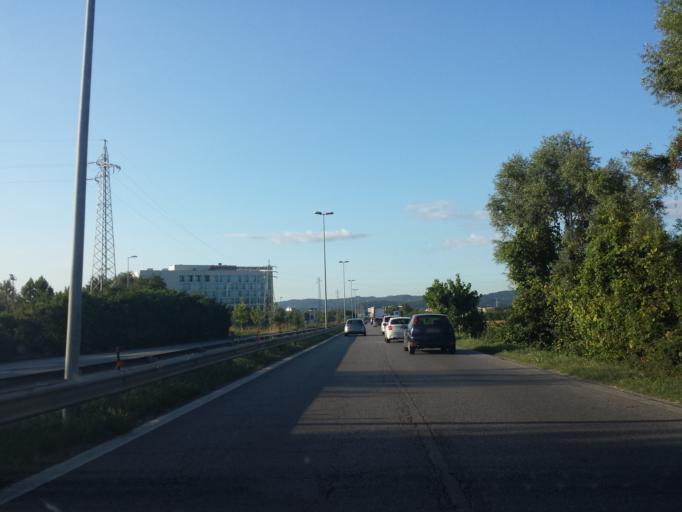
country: IT
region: Veneto
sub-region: Provincia di Vicenza
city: Creazzo
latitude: 45.5453
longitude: 11.5089
